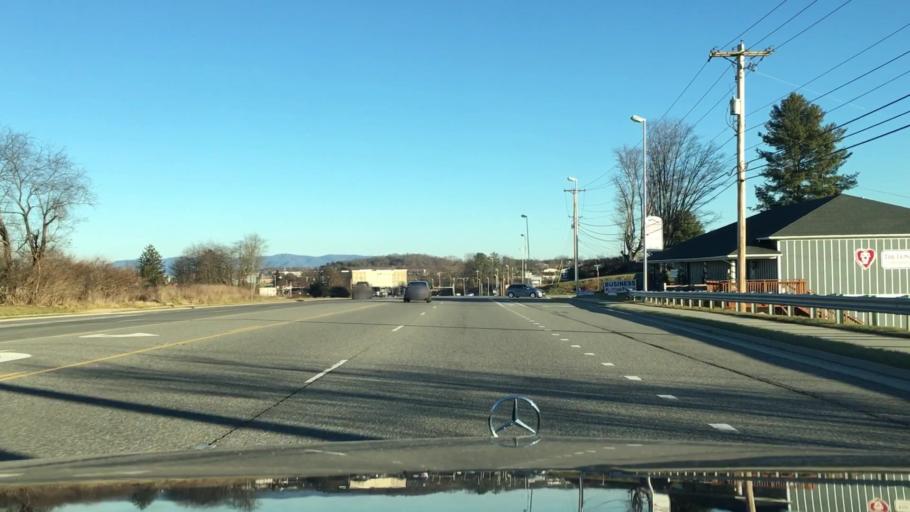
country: US
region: Virginia
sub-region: Montgomery County
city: Merrimac
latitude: 37.1628
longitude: -80.4358
